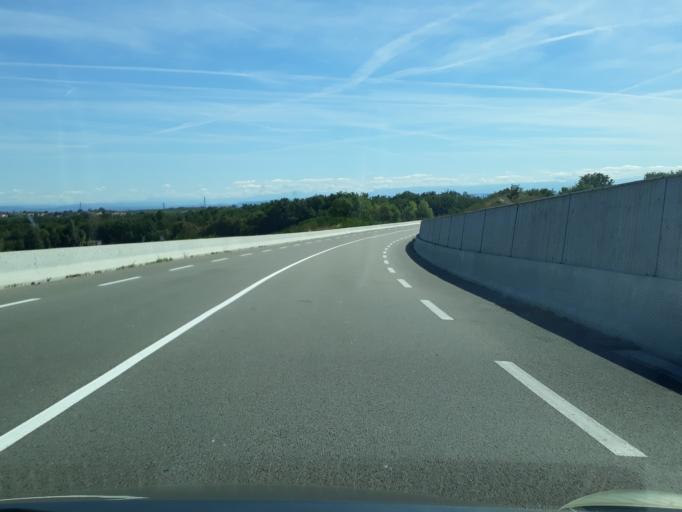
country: FR
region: Rhone-Alpes
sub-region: Departement de l'Ardeche
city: Davezieux
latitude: 45.2619
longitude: 4.7124
